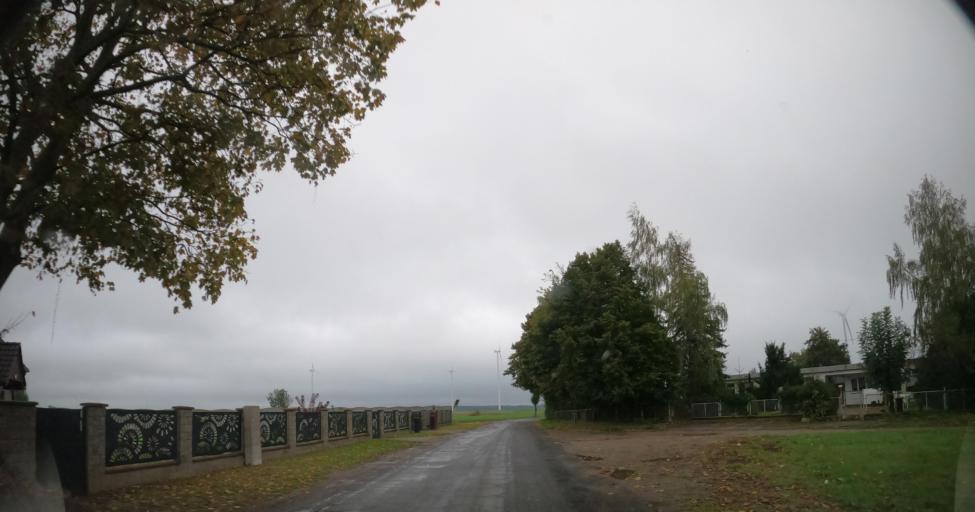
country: PL
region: West Pomeranian Voivodeship
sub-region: Powiat pyrzycki
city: Kozielice
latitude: 53.0894
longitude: 14.7730
